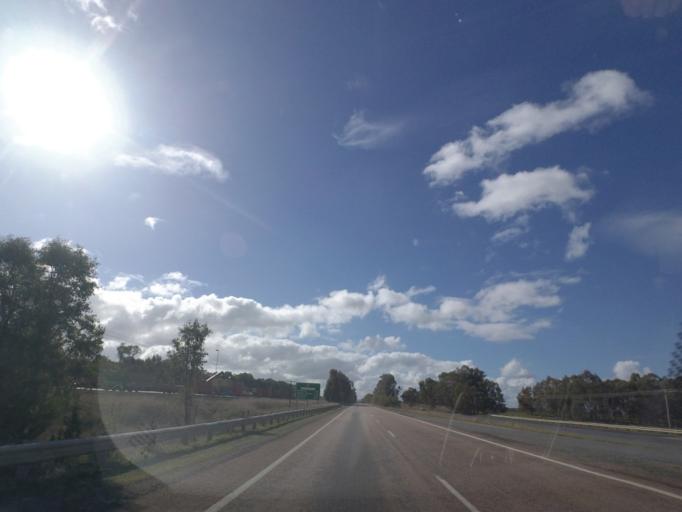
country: AU
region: New South Wales
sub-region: Albury Municipality
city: Lavington
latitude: -35.9900
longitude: 146.9956
